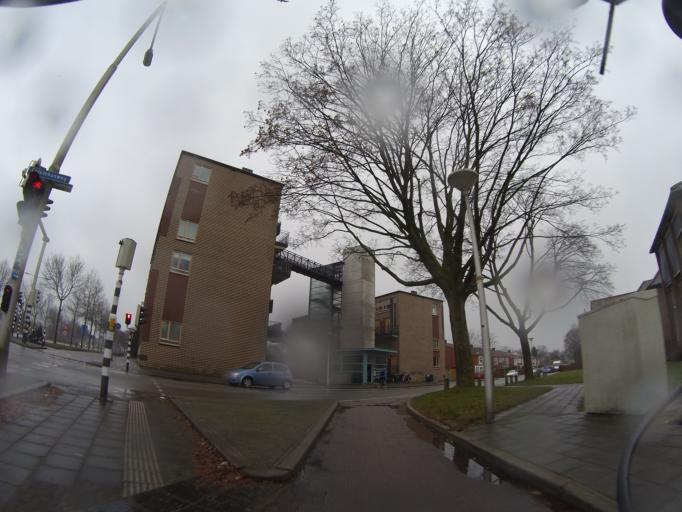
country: NL
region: Utrecht
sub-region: Gemeente Amersfoort
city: Randenbroek
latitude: 52.1605
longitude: 5.4043
